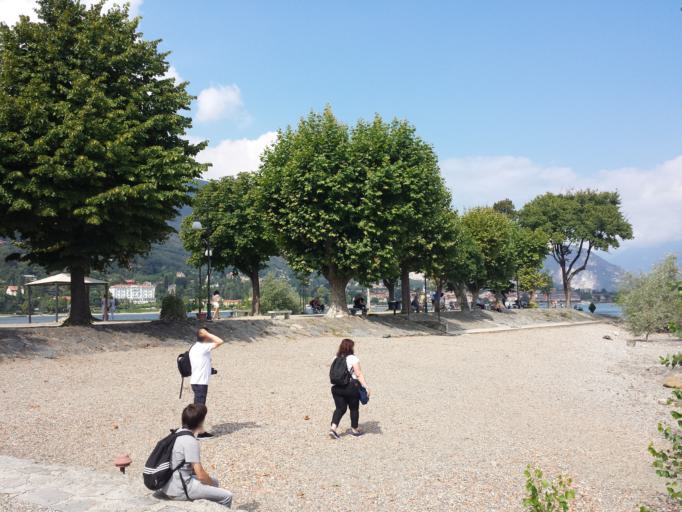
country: IT
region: Piedmont
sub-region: Provincia Verbano-Cusio-Ossola
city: Baveno
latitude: 45.9016
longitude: 8.5199
